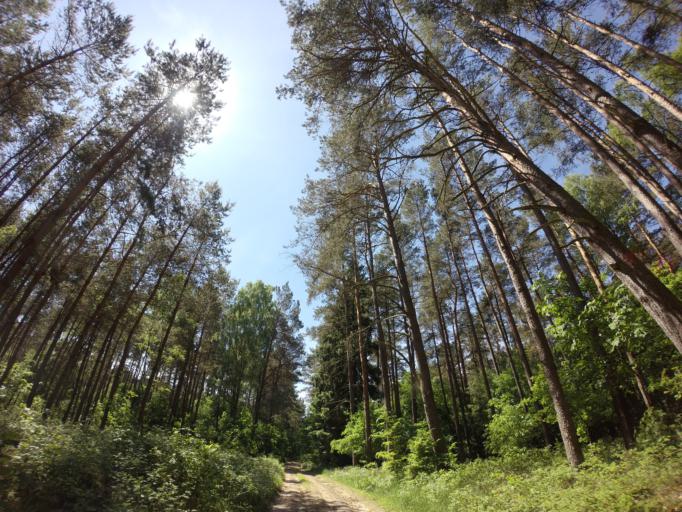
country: PL
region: West Pomeranian Voivodeship
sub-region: Powiat choszczenski
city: Drawno
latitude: 53.2614
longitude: 15.7281
